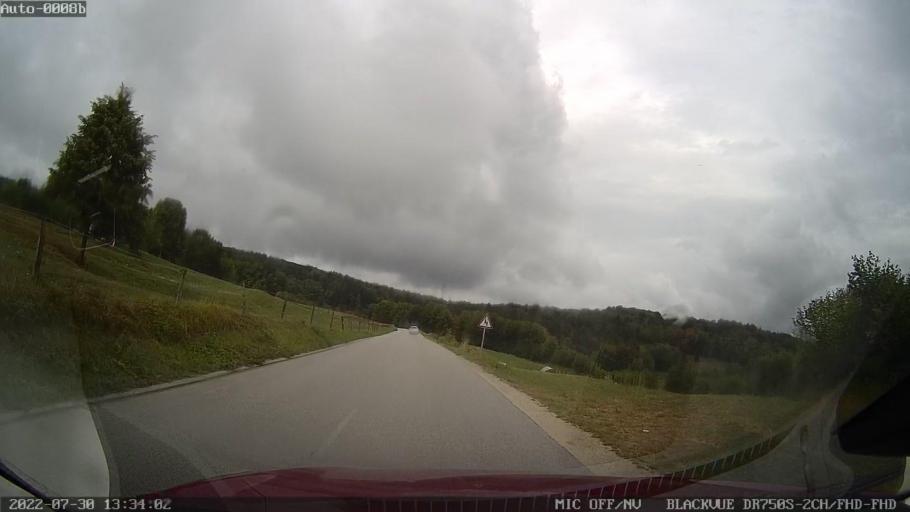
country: SI
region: Zuzemberk
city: Zuzemberk
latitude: 45.8559
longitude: 14.9335
